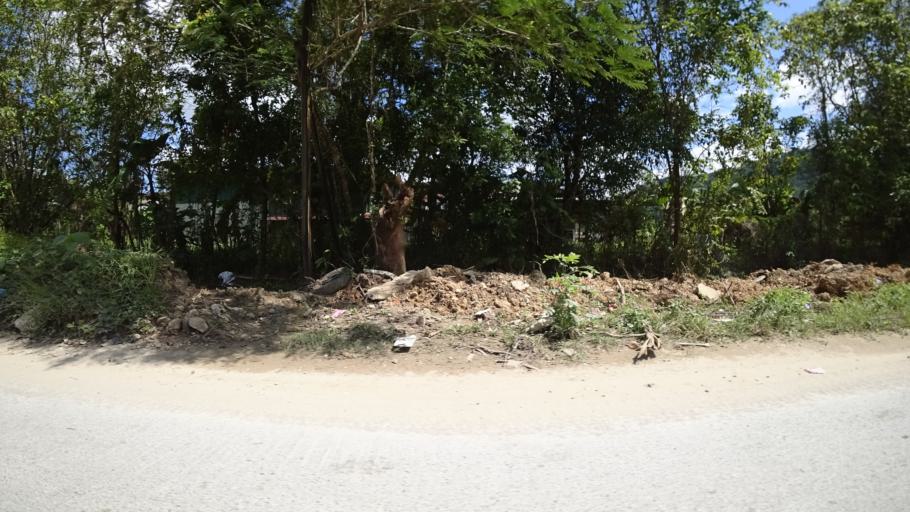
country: MY
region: Sarawak
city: Limbang
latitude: 4.7429
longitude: 115.0009
